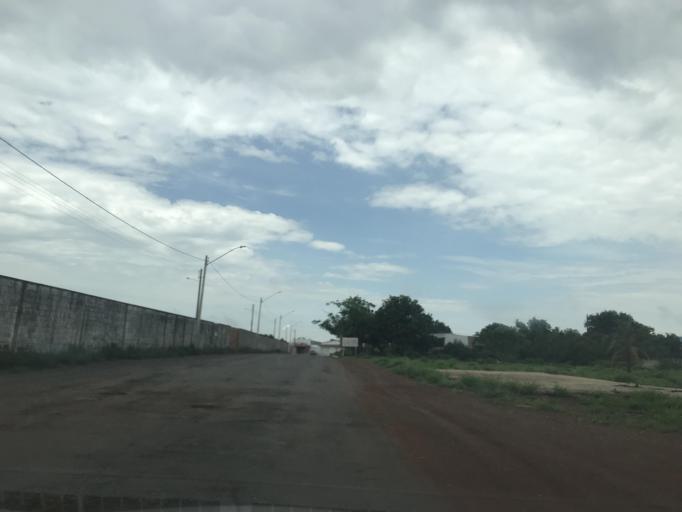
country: BR
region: Goias
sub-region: Luziania
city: Luziania
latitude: -16.2575
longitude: -47.9740
